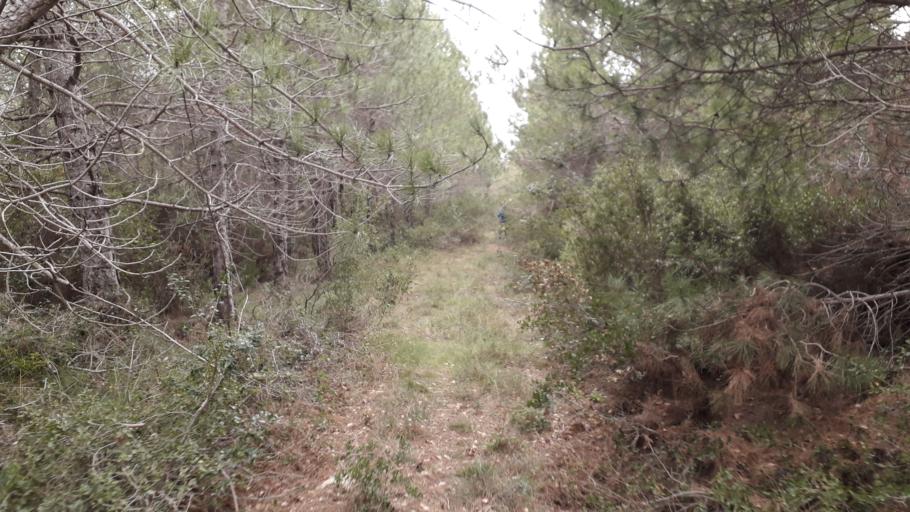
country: ES
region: Catalonia
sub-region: Provincia de Barcelona
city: Bellprat
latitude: 41.4864
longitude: 1.4749
